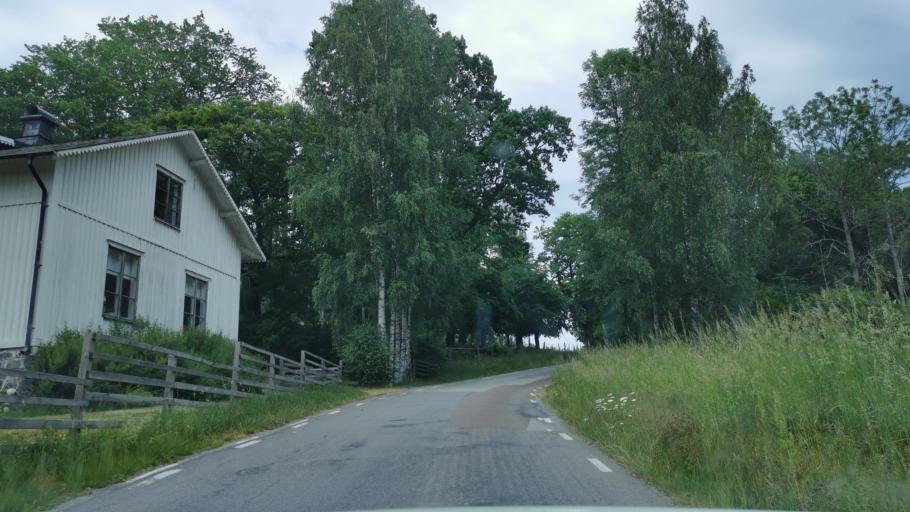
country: SE
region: Vaestra Goetaland
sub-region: Bengtsfors Kommun
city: Dals Langed
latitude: 58.8461
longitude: 12.4076
